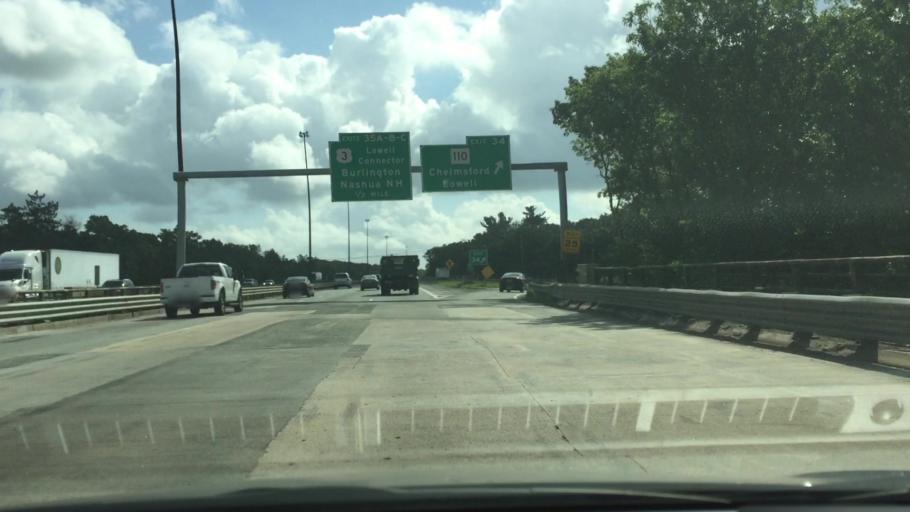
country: US
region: Massachusetts
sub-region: Middlesex County
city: Chelmsford
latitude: 42.6051
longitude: -71.3447
